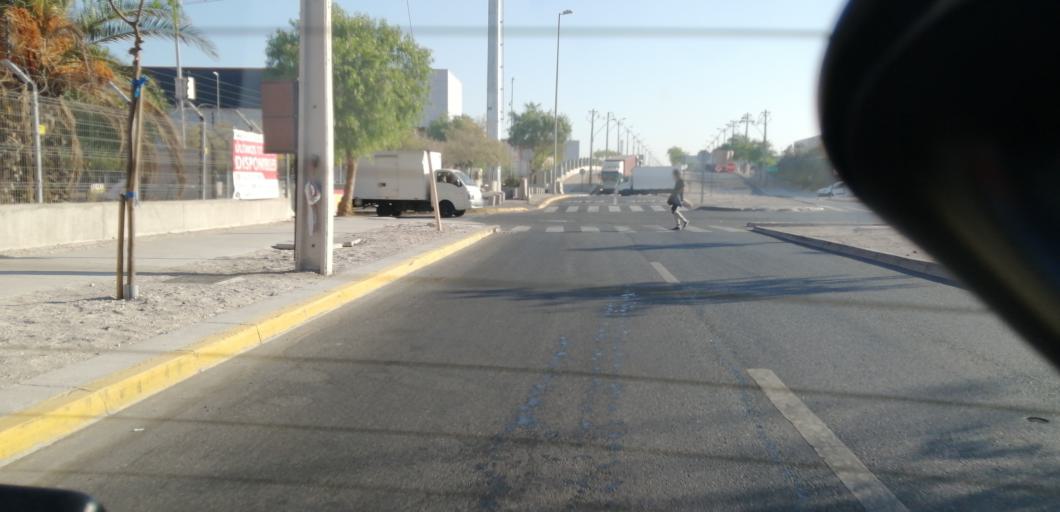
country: CL
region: Santiago Metropolitan
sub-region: Provincia de Santiago
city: Lo Prado
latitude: -33.4326
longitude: -70.7884
